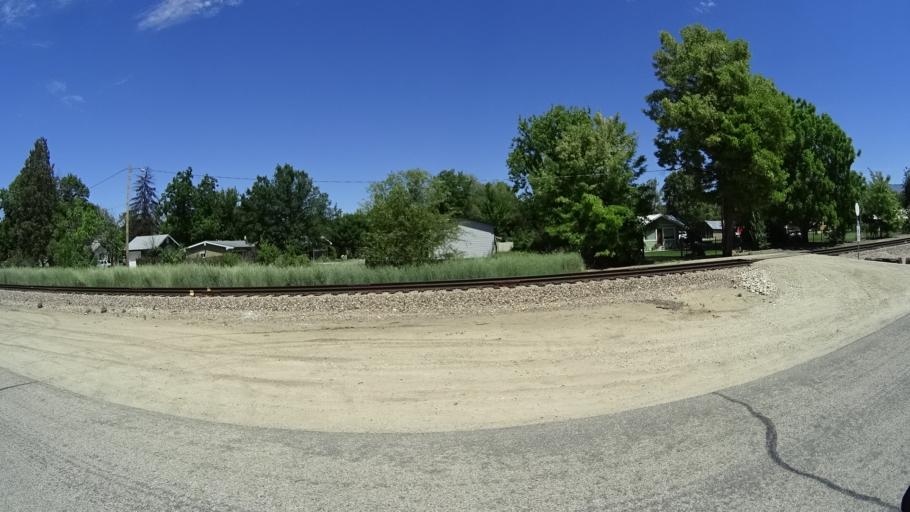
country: US
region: Idaho
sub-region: Ada County
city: Garden City
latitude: 43.6044
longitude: -116.2375
